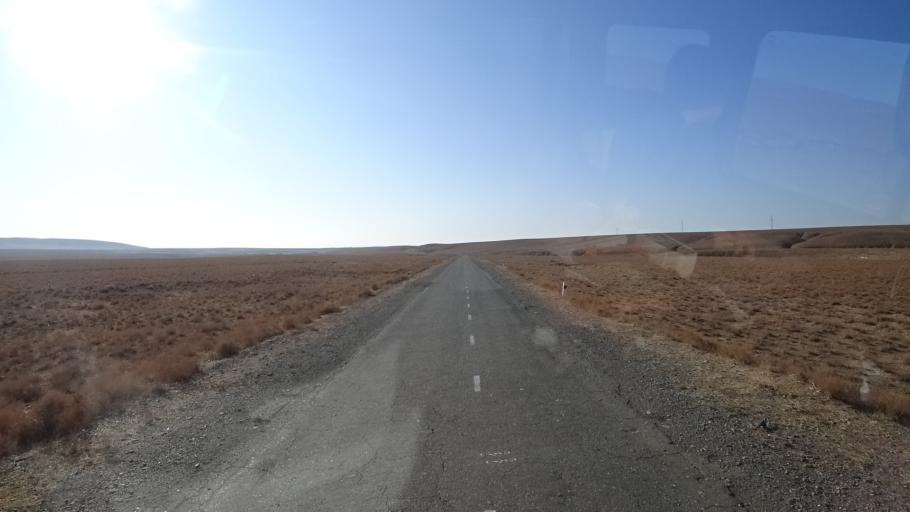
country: UZ
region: Navoiy
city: Beshrabot
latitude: 40.2605
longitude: 65.4865
